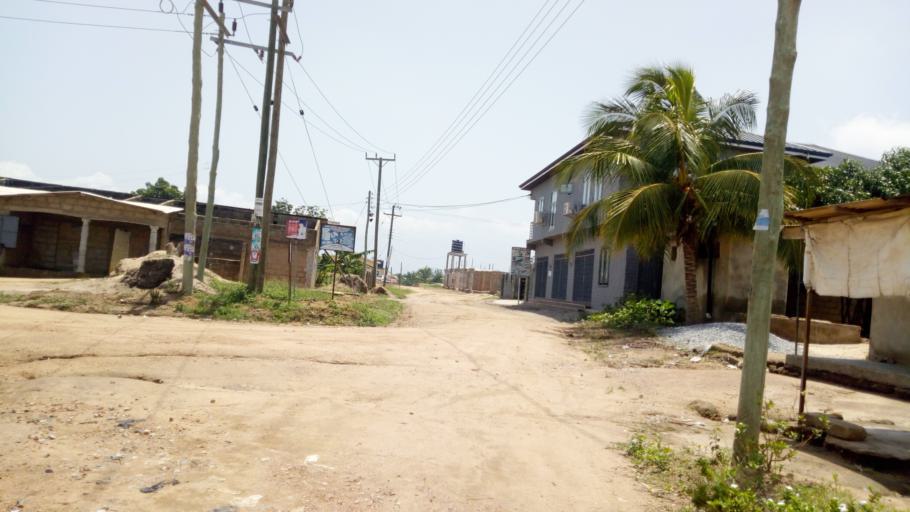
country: GH
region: Central
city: Kasoa
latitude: 5.5035
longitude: -0.4512
